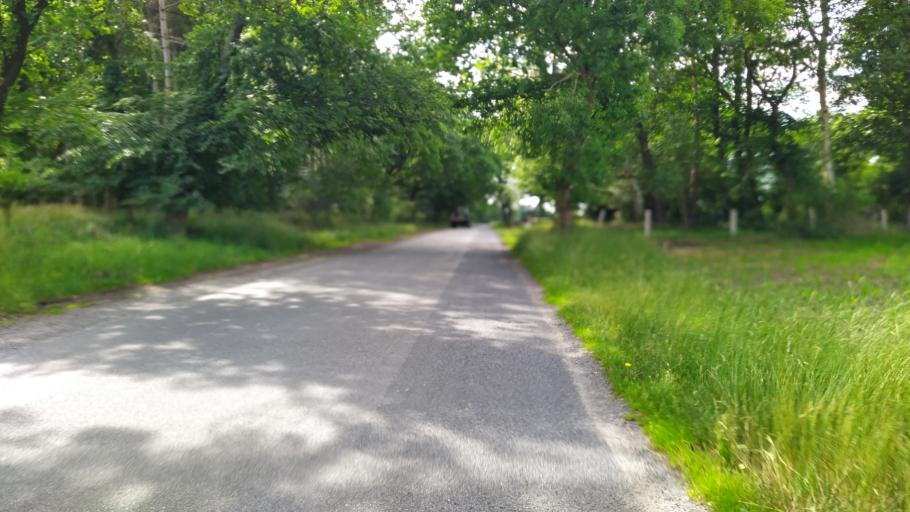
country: DE
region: Lower Saxony
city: Armstorf
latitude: 53.6076
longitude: 9.0425
